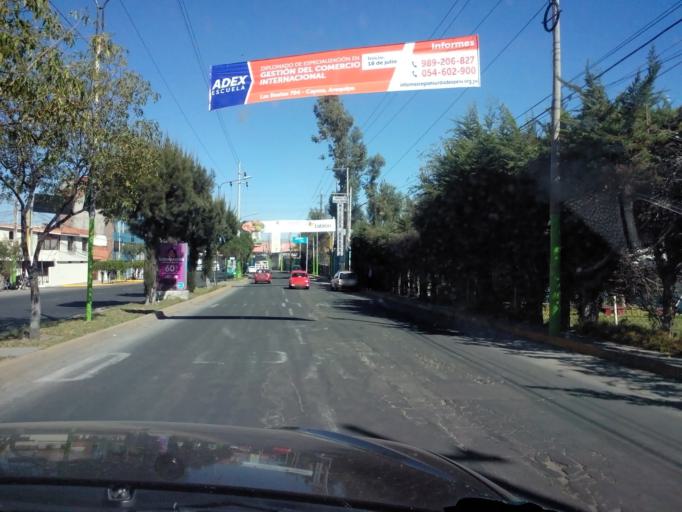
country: PE
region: Arequipa
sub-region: Provincia de Arequipa
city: Arequipa
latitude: -16.3820
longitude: -71.5566
